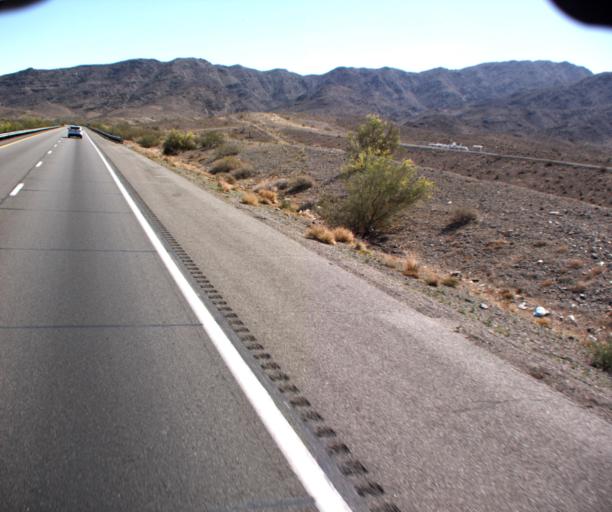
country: US
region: Arizona
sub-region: La Paz County
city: Ehrenberg
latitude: 33.6325
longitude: -114.4003
